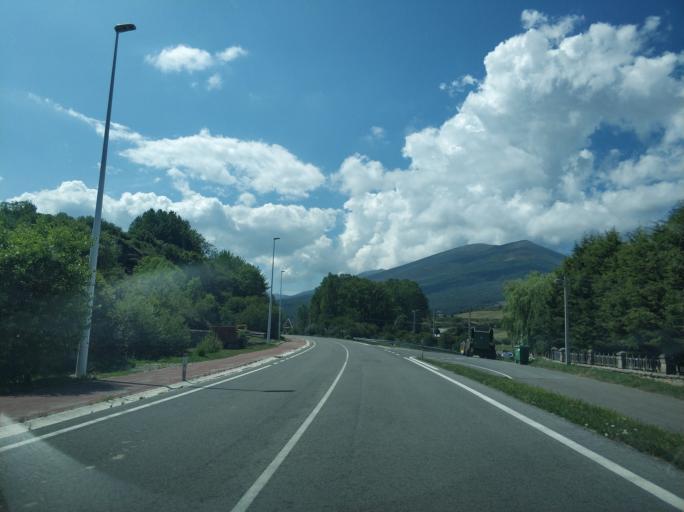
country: ES
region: Cantabria
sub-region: Provincia de Cantabria
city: Villaescusa
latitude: 43.0216
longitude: -4.2281
